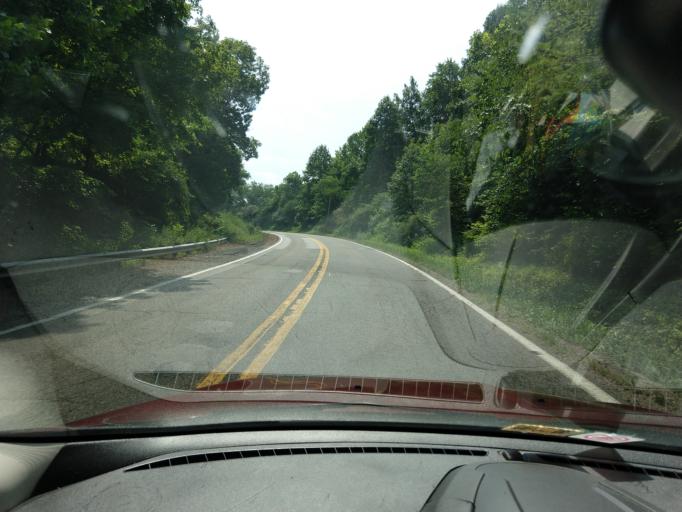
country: US
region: West Virginia
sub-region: Jackson County
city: Ripley
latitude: 38.8411
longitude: -81.7955
